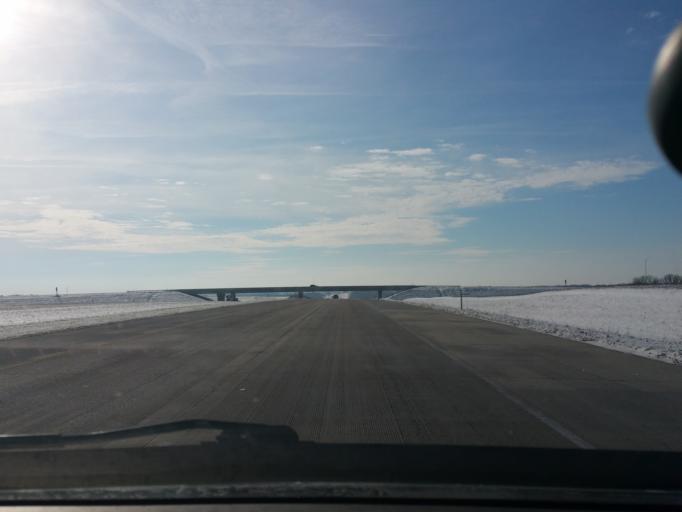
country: US
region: Iowa
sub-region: Warren County
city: Norwalk
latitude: 41.4863
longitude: -93.7805
